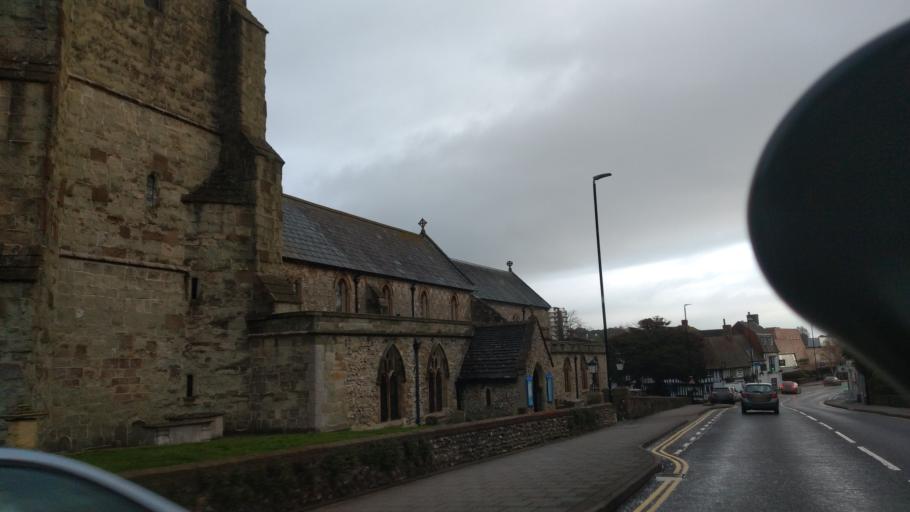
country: GB
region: England
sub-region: East Sussex
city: Eastbourne
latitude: 50.7724
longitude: 0.2654
